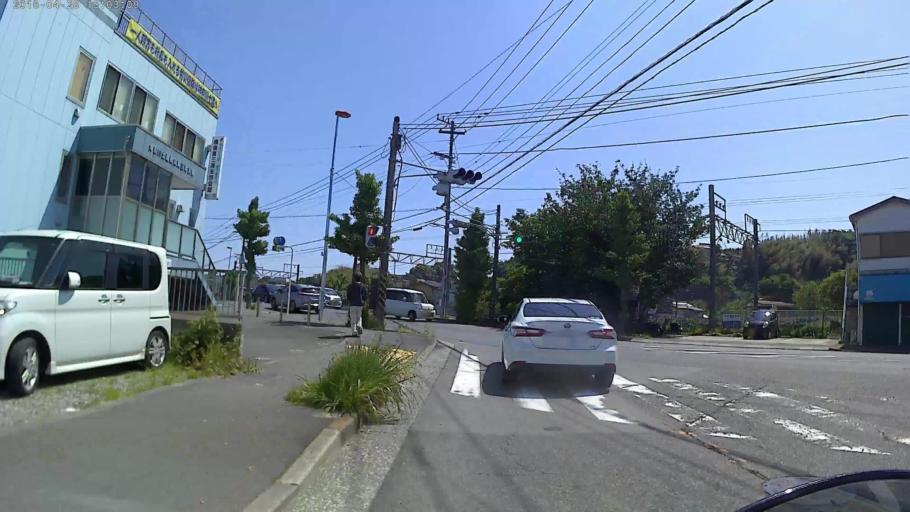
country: JP
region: Kanagawa
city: Yokosuka
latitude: 35.2522
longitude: 139.6778
